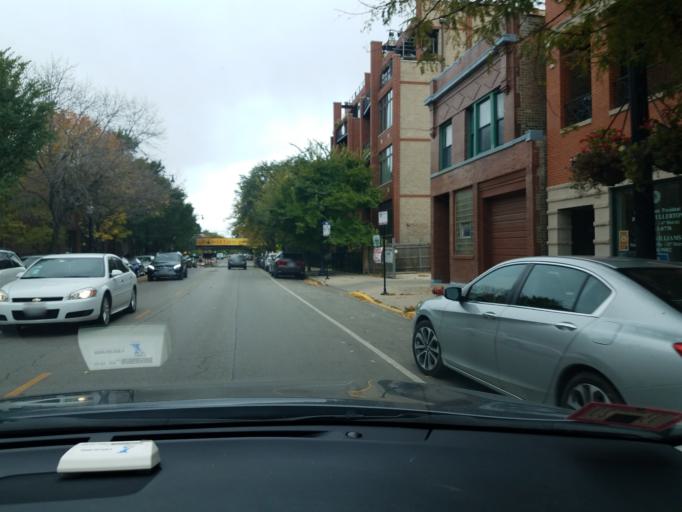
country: US
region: Illinois
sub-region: Cook County
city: Lincolnwood
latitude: 41.9397
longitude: -87.6731
